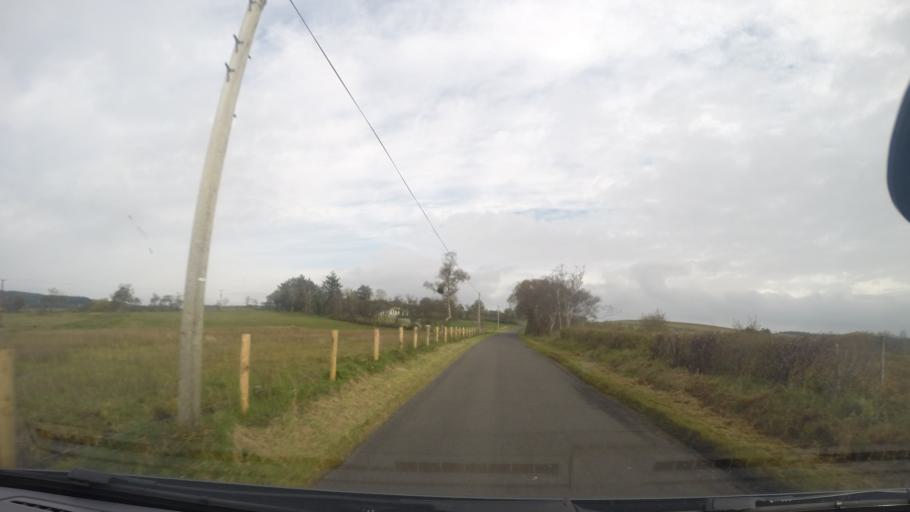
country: IE
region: Ulster
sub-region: County Donegal
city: Ballyshannon
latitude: 54.4235
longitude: -7.9951
